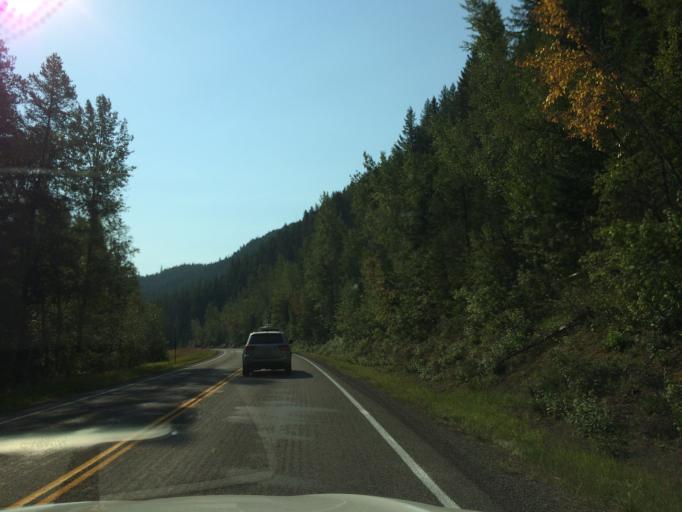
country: US
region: Montana
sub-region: Flathead County
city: Columbia Falls
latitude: 48.4920
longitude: -113.8798
